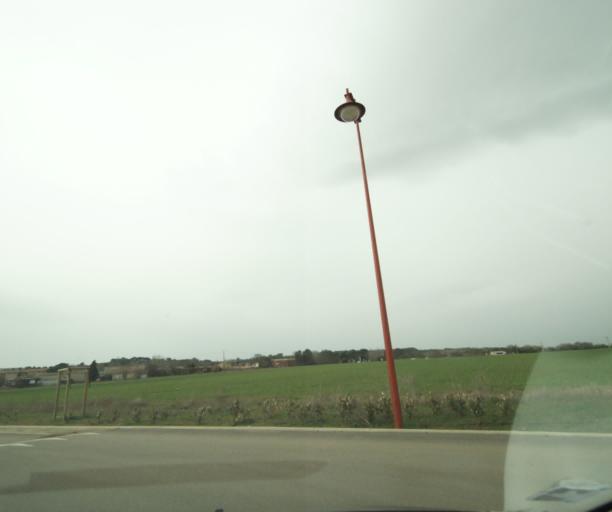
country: FR
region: Provence-Alpes-Cote d'Azur
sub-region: Departement des Bouches-du-Rhone
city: Trets
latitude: 43.4533
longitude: 5.6782
